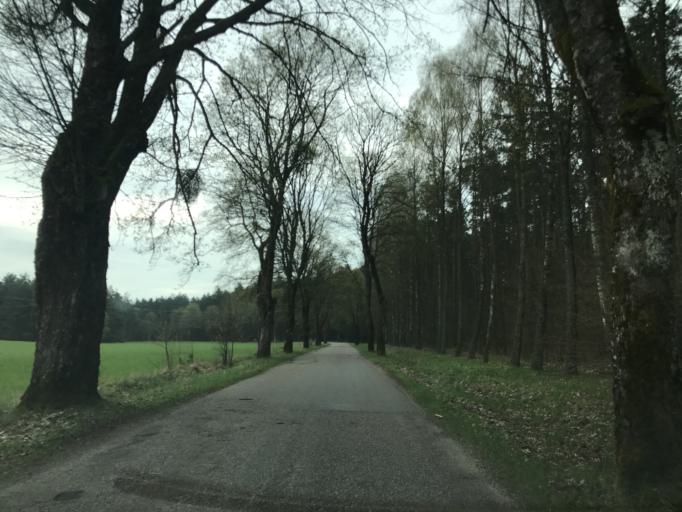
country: PL
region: Warmian-Masurian Voivodeship
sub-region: Powiat olsztynski
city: Olsztynek
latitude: 53.6114
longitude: 20.2537
